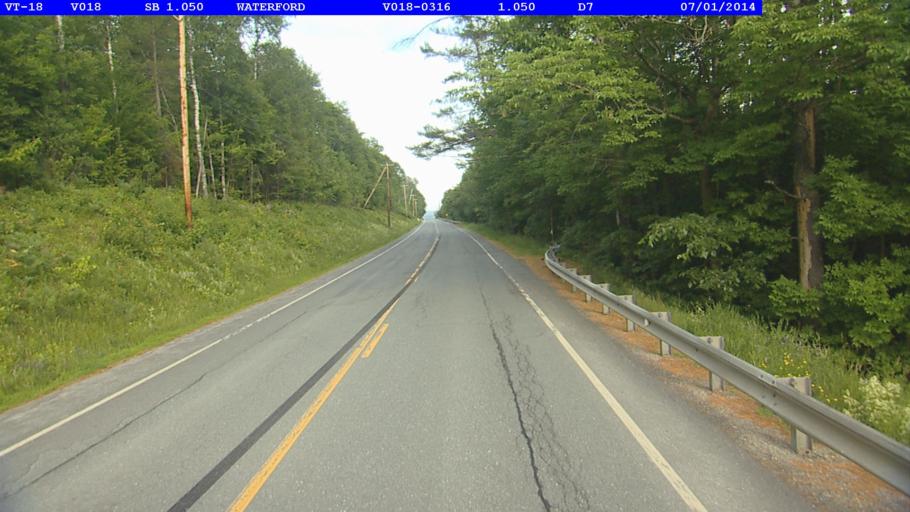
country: US
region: Vermont
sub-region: Caledonia County
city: Saint Johnsbury
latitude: 44.3531
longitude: -71.9035
